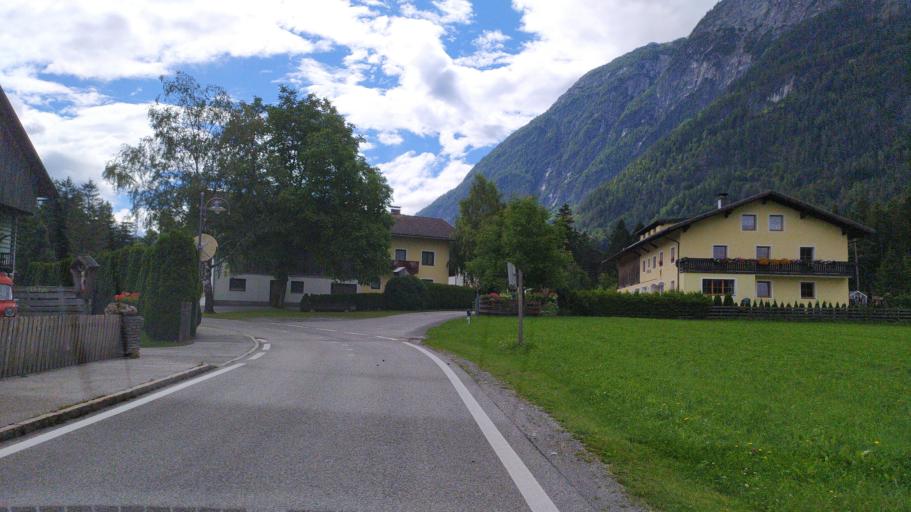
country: AT
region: Tyrol
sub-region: Politischer Bezirk Lienz
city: Lavant
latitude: 46.7913
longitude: 12.8597
